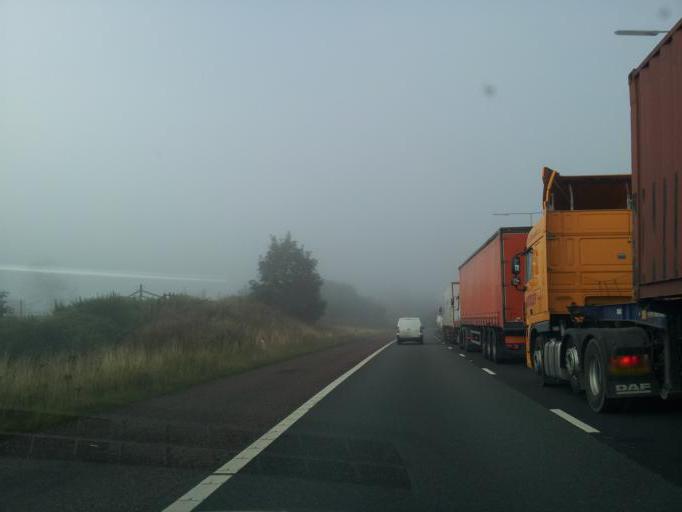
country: GB
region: England
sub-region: Borough of Rochdale
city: Milnrow
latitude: 53.5949
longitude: -2.1274
